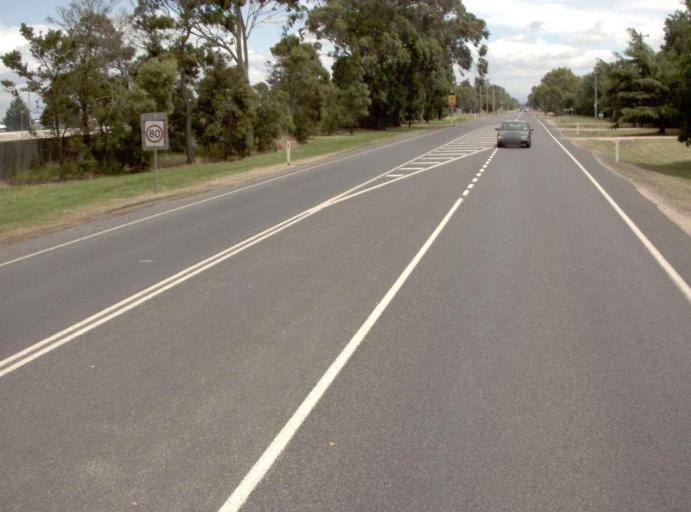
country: AU
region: Victoria
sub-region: Wellington
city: Sale
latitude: -38.0903
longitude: 147.0645
